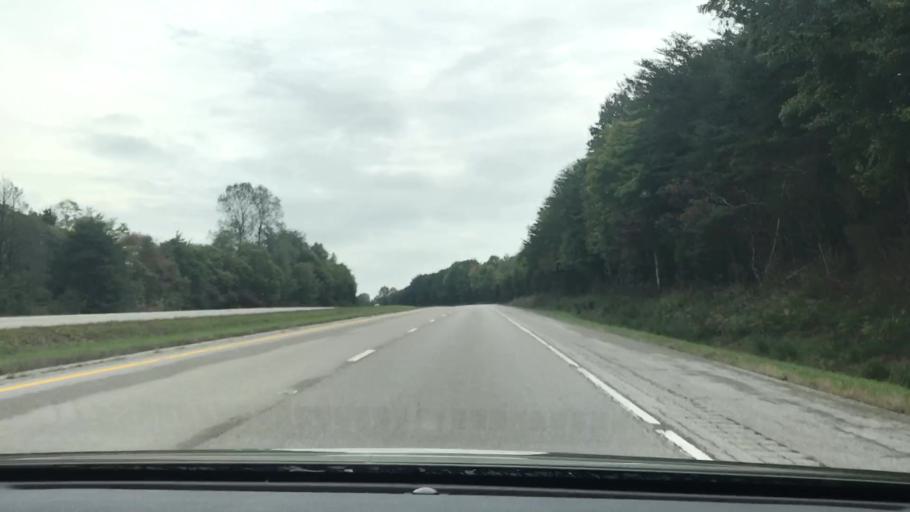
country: US
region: Kentucky
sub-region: Metcalfe County
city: Edmonton
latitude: 37.0079
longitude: -85.5822
